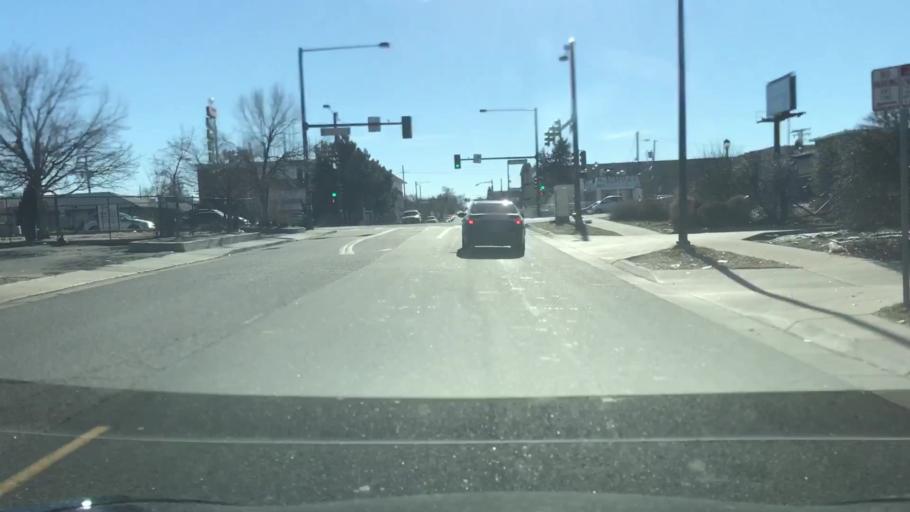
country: US
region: Colorado
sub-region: Adams County
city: Aurora
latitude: 39.7408
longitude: -104.8847
